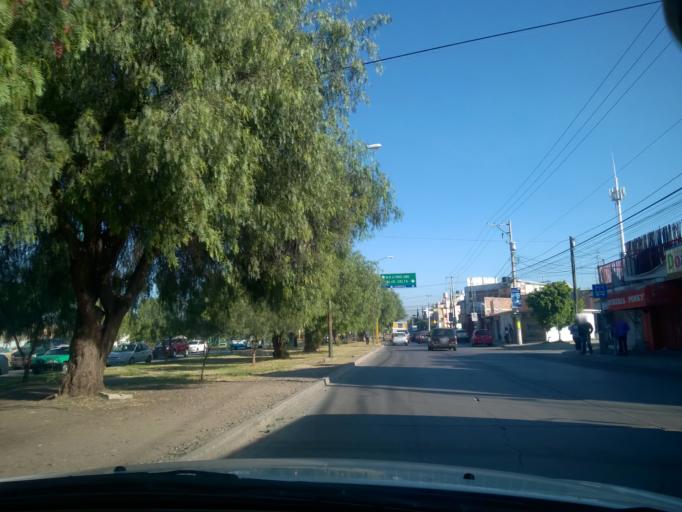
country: MX
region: Guanajuato
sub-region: Leon
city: San Jose de Duran (Los Troncoso)
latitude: 21.0831
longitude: -101.6436
